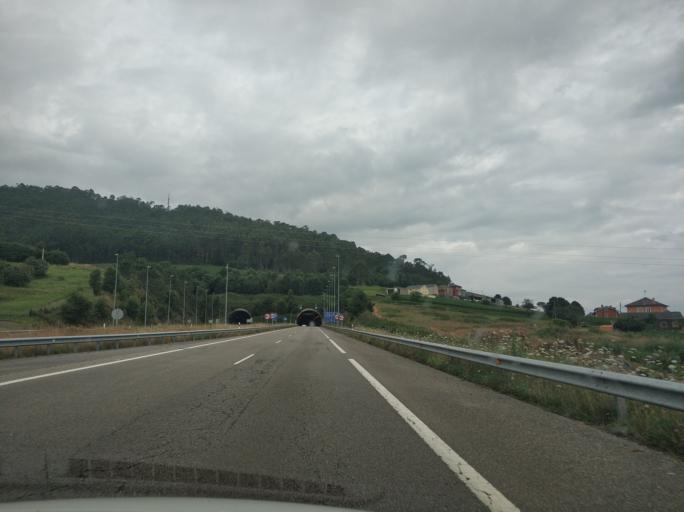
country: ES
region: Asturias
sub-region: Province of Asturias
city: Coana
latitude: 43.5344
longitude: -6.7443
